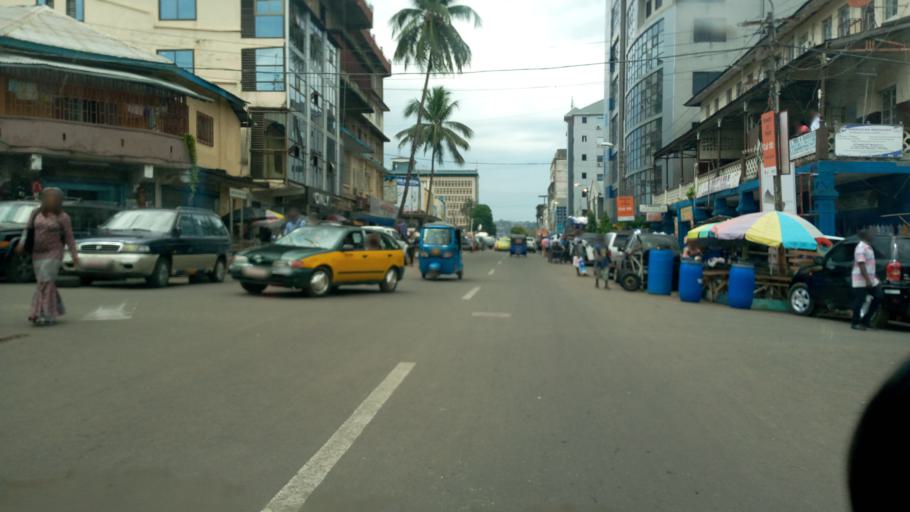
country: SL
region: Western Area
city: Freetown
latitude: 8.4908
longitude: -13.2335
